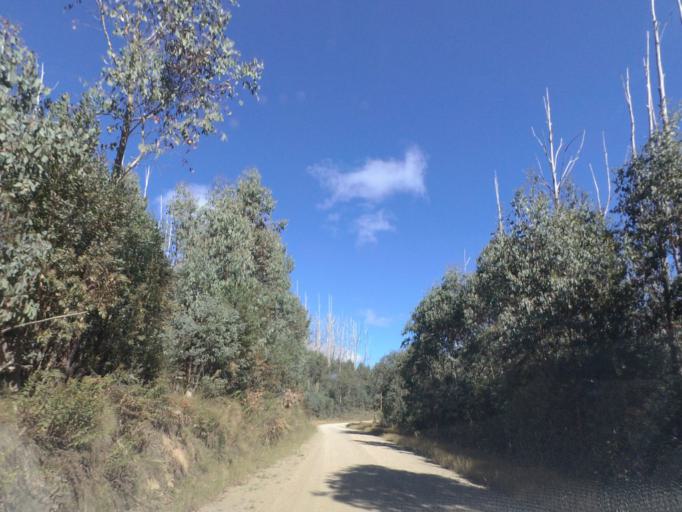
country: AU
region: Victoria
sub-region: Murrindindi
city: Alexandra
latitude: -37.4178
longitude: 145.8000
